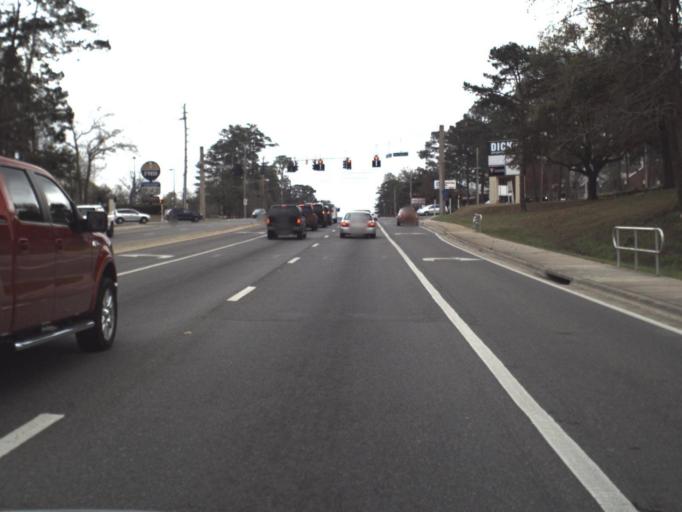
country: US
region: Florida
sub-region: Leon County
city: Tallahassee
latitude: 30.4326
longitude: -84.2507
